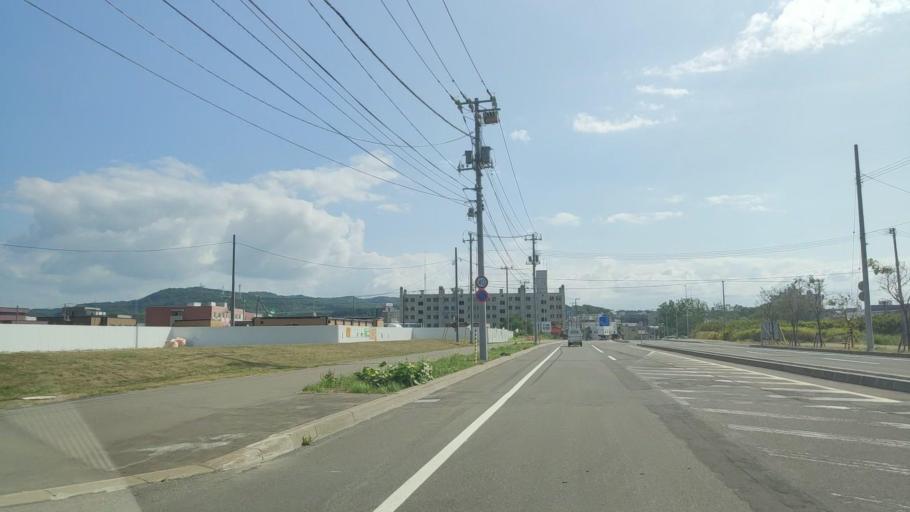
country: JP
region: Hokkaido
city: Rumoi
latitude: 43.9443
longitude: 141.6478
